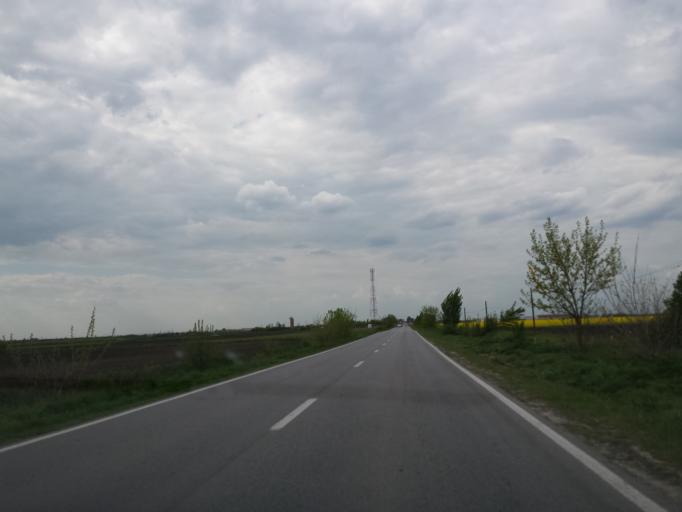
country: RO
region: Timis
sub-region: Comuna Sanpetru Mare
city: Sanpetru Mare
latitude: 46.0424
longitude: 20.6527
